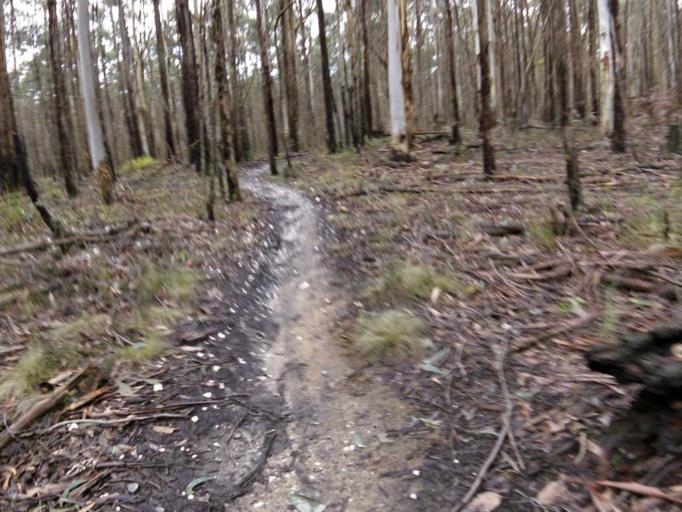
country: AU
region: Victoria
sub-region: Moorabool
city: Bacchus Marsh
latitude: -37.4225
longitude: 144.4824
